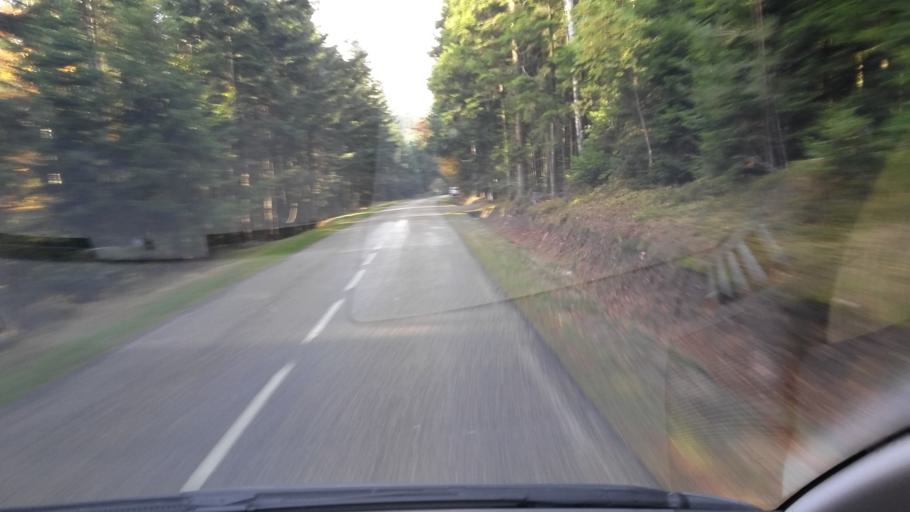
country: FR
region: Lorraine
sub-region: Departement de la Moselle
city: Dabo
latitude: 48.6719
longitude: 7.2539
